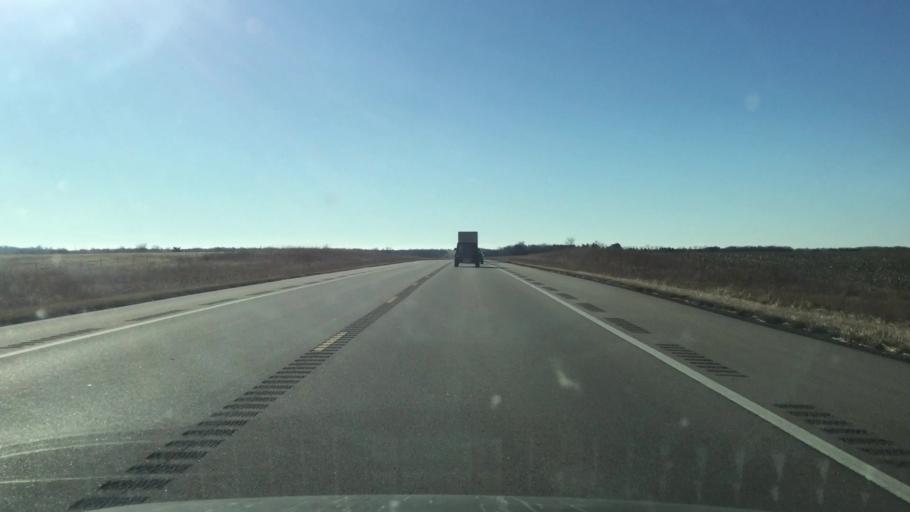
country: US
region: Kansas
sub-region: Allen County
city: Iola
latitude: 38.0494
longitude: -95.3805
